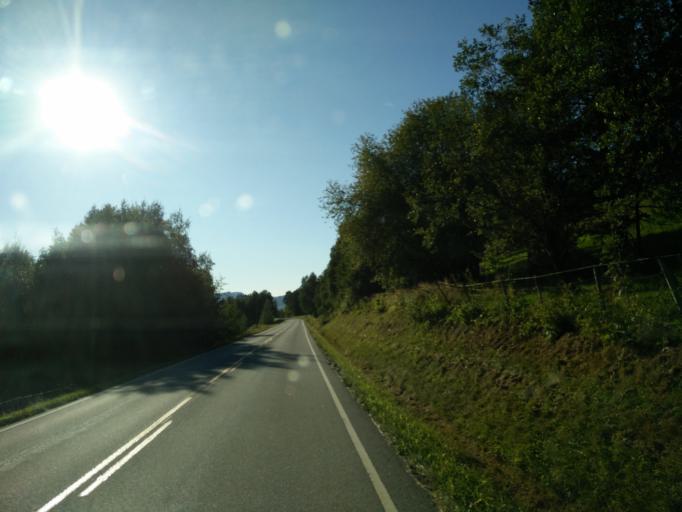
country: NO
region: More og Romsdal
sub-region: Halsa
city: Liaboen
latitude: 63.0842
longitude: 8.4034
